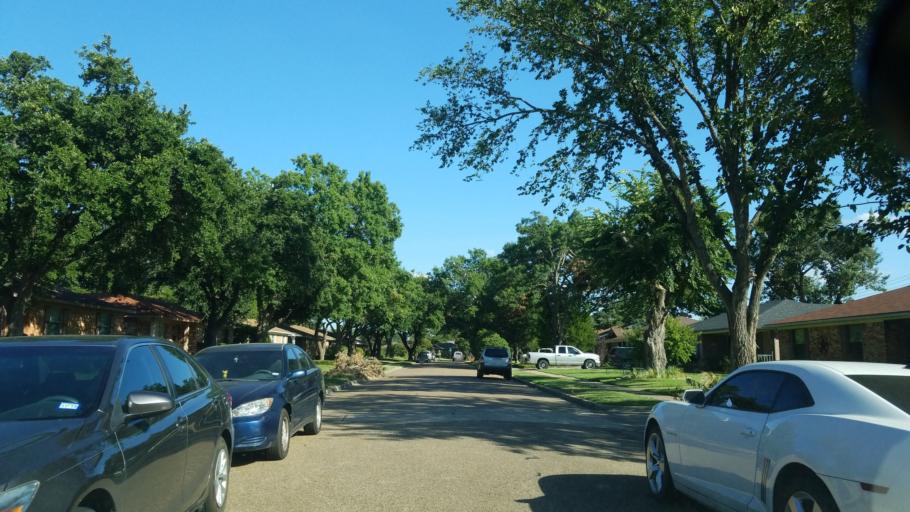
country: US
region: Texas
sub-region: Dallas County
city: Highland Park
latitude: 32.7908
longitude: -96.7019
